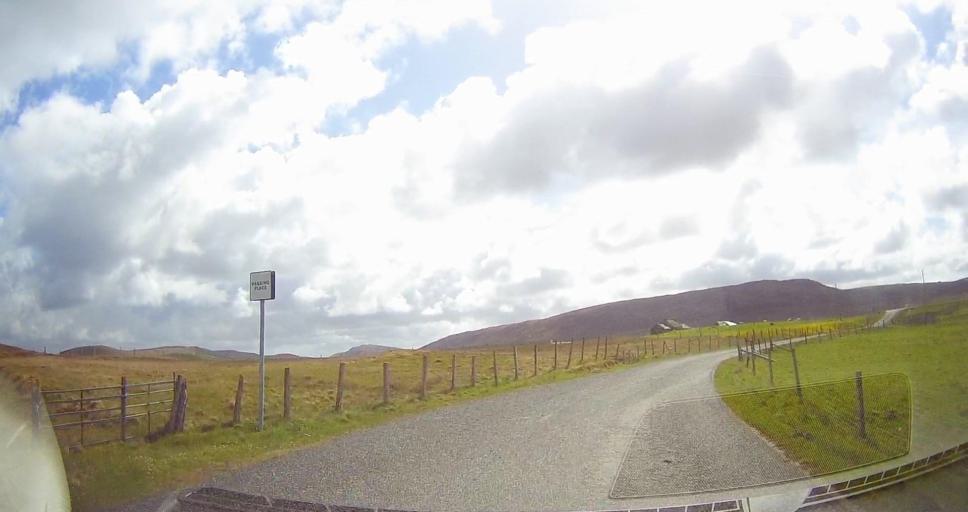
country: GB
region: Scotland
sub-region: Shetland Islands
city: Lerwick
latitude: 60.5897
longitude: -1.3298
